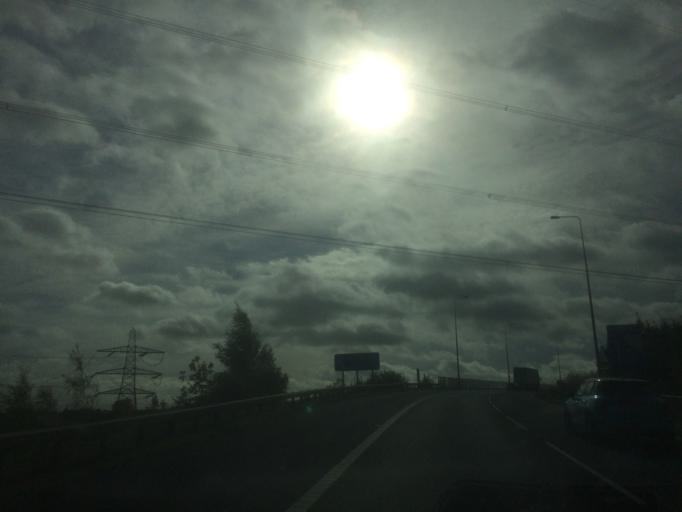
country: GB
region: England
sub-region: City and Borough of Wakefield
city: Ferrybridge
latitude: 53.7175
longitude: -1.2887
